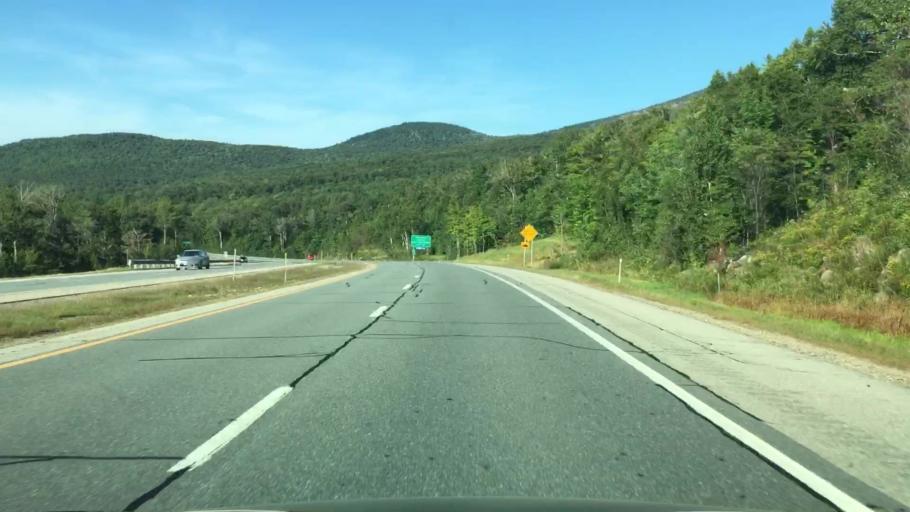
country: US
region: New Hampshire
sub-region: Grafton County
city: Deerfield
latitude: 44.1856
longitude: -71.6840
